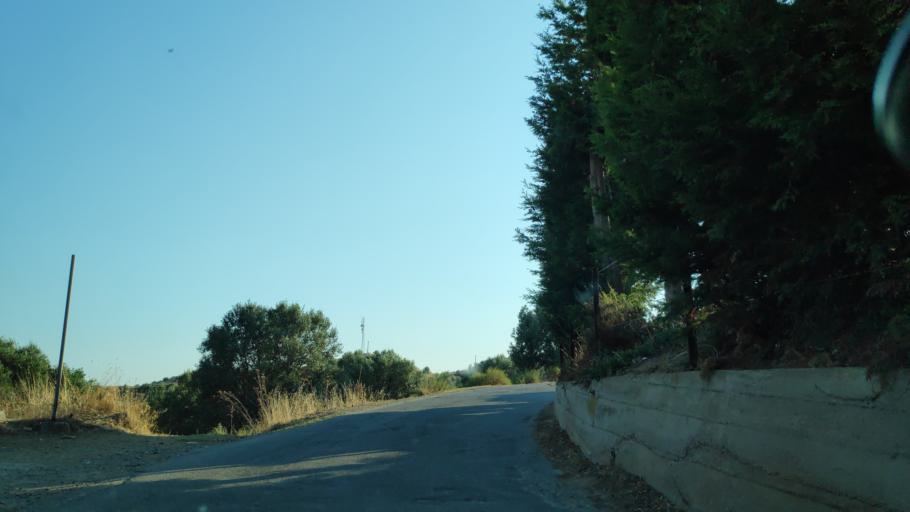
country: IT
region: Calabria
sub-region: Provincia di Reggio Calabria
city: Monasterace Marina
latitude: 38.4481
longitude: 16.5709
